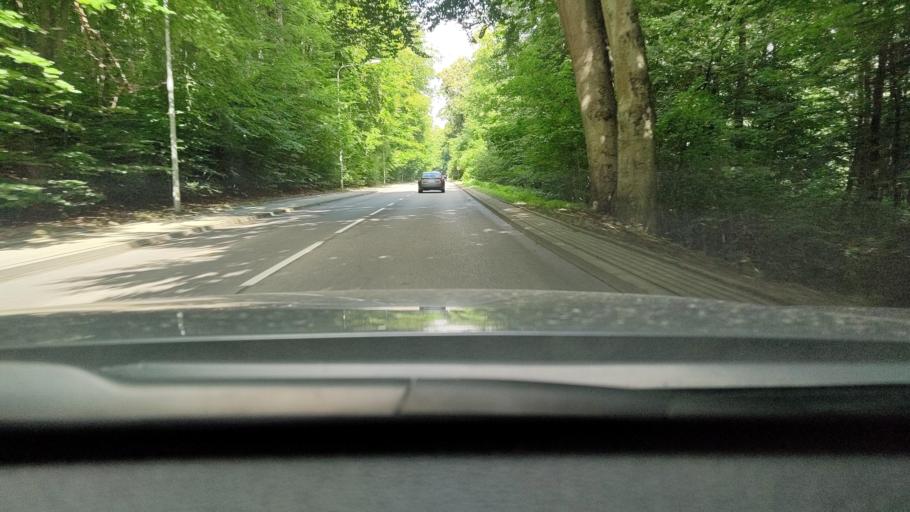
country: PL
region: Pomeranian Voivodeship
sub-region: Powiat wejherowski
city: Wejherowo
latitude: 54.5927
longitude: 18.2375
